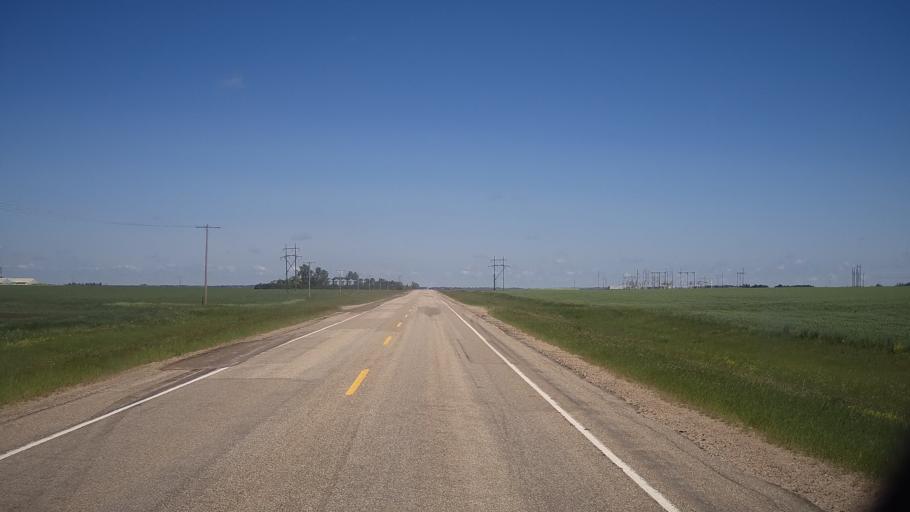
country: CA
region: Saskatchewan
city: Saskatoon
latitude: 51.9756
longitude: -106.0753
